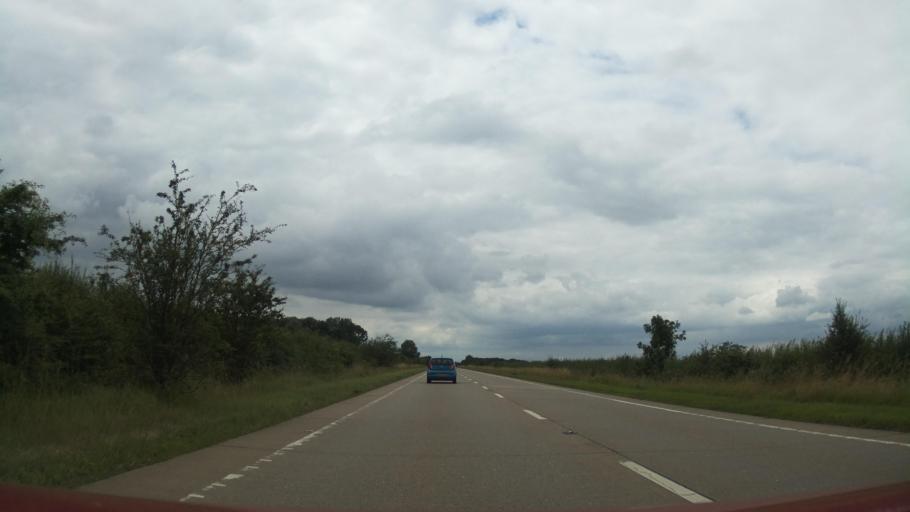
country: GB
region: England
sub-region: Lincolnshire
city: Long Bennington
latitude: 52.9364
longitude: -0.8252
